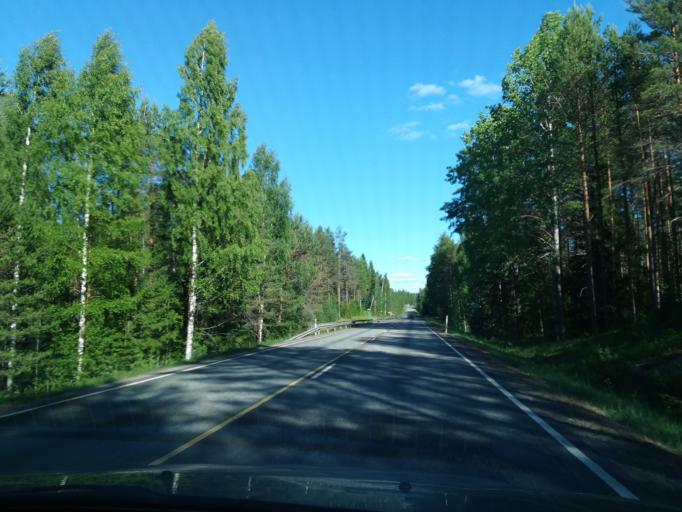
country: FI
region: South Karelia
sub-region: Imatra
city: Ruokolahti
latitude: 61.3658
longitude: 28.6857
